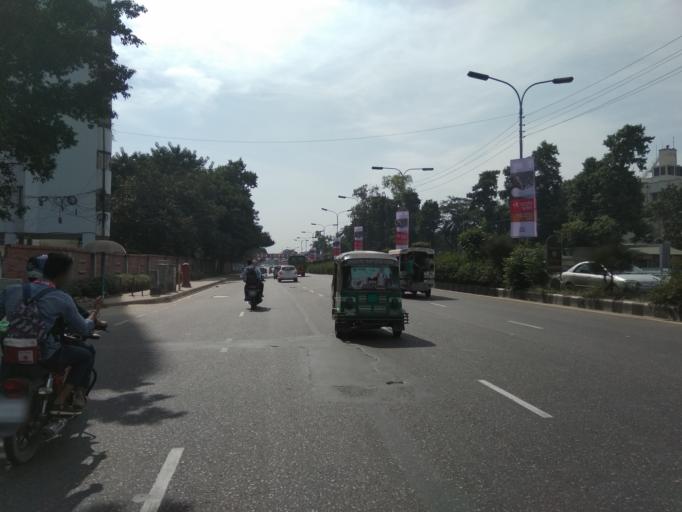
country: BD
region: Dhaka
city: Azimpur
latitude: 23.7725
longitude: 90.3901
